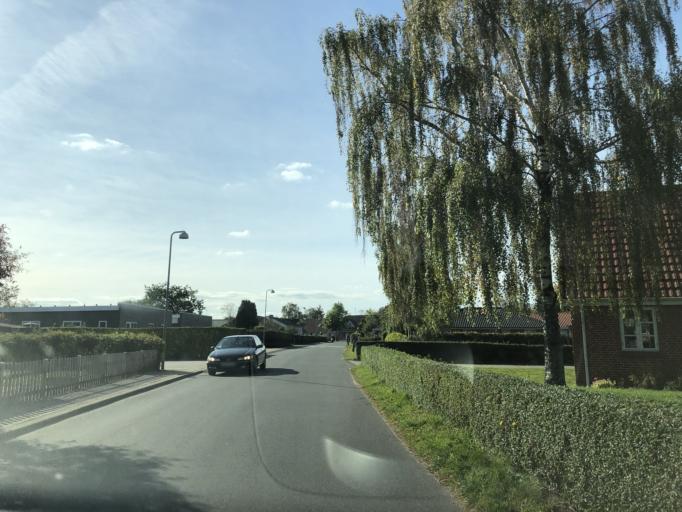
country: DK
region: Central Jutland
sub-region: Syddjurs Kommune
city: Hornslet
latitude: 56.3125
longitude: 10.3113
